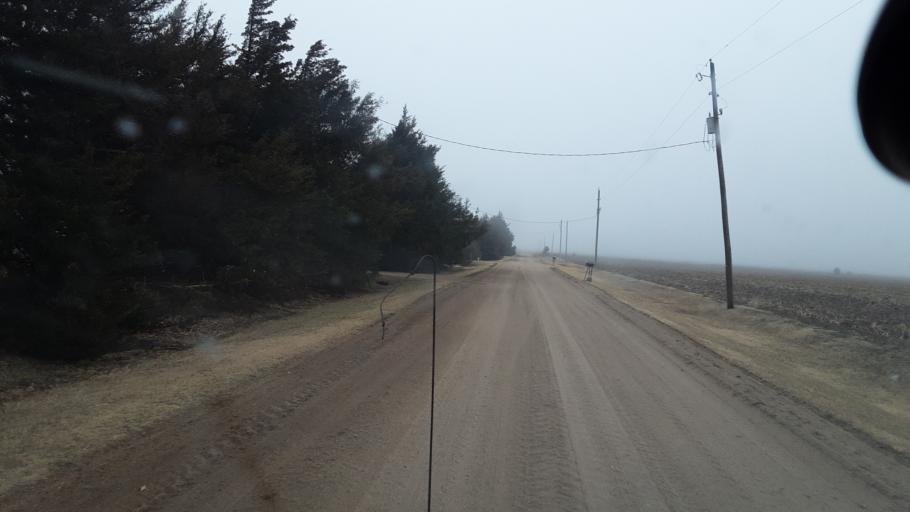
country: US
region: Kansas
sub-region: Reno County
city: South Hutchinson
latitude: 37.9842
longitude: -97.9705
